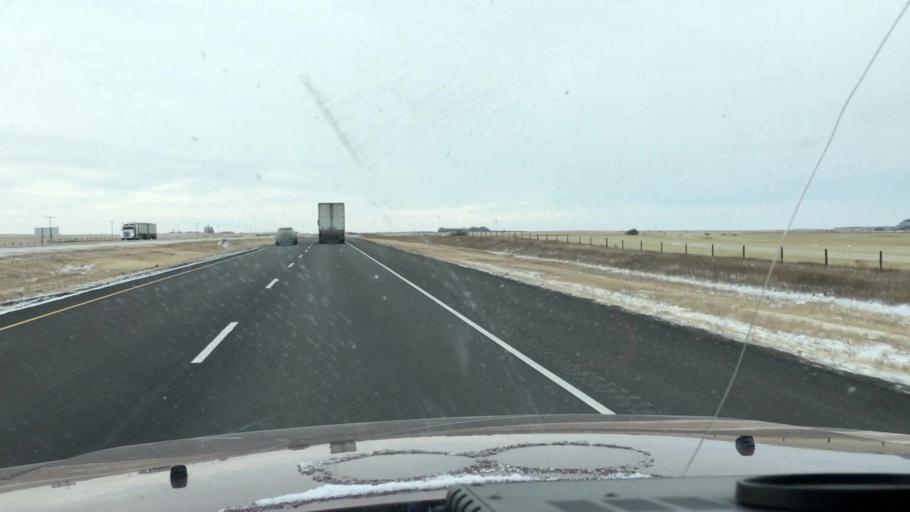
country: CA
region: Saskatchewan
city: Saskatoon
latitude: 51.7999
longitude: -106.4894
